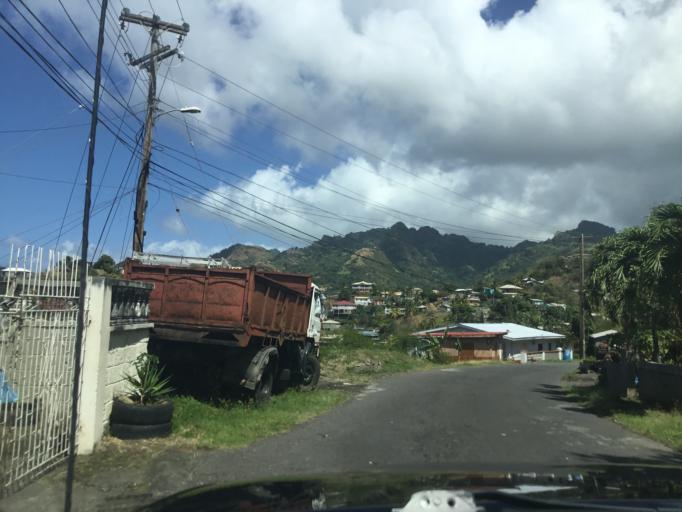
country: VC
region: Saint George
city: Kingstown Park
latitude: 13.1614
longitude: -61.2386
